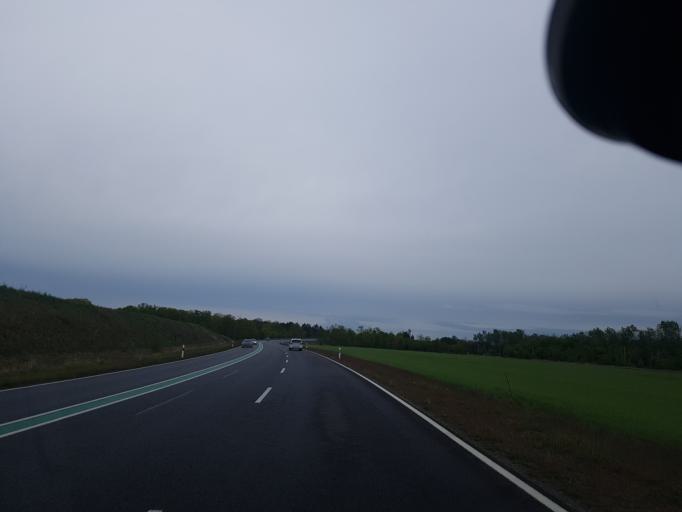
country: DE
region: Brandenburg
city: Drebkau
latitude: 51.6346
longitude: 14.1945
